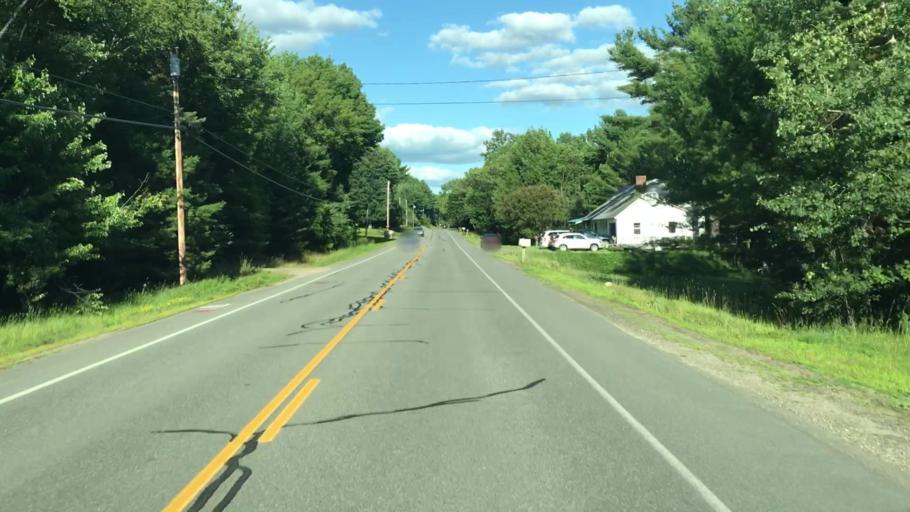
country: US
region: Maine
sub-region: Penobscot County
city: Lincoln
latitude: 45.3749
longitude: -68.4836
